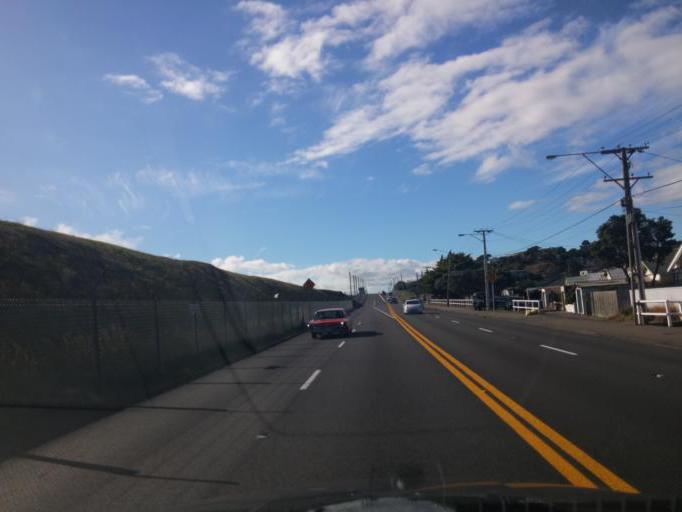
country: NZ
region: Wellington
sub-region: Wellington City
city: Wellington
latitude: -41.3223
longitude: 174.8091
